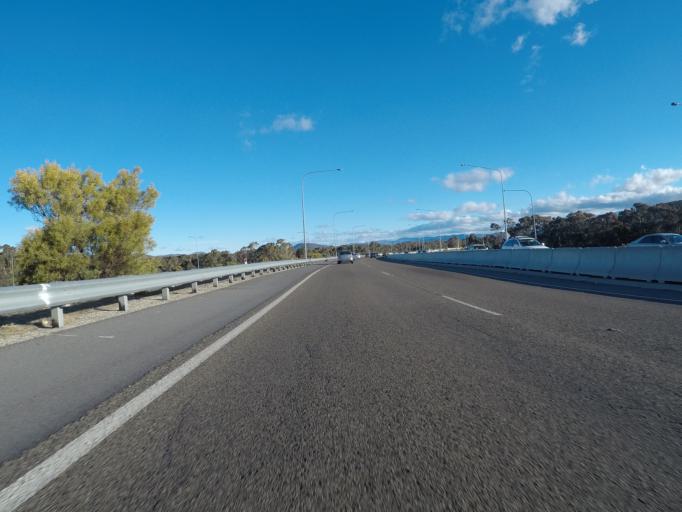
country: AU
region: Australian Capital Territory
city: Acton
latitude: -35.2817
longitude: 149.0863
